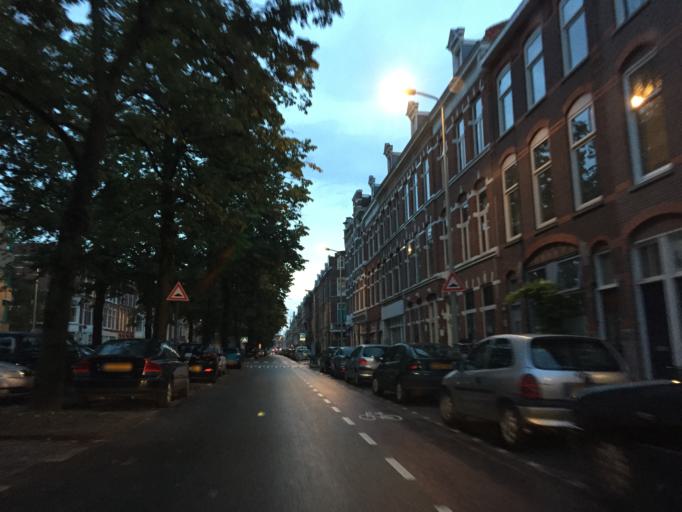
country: NL
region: South Holland
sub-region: Gemeente Den Haag
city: The Hague
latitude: 52.0744
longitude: 4.2835
